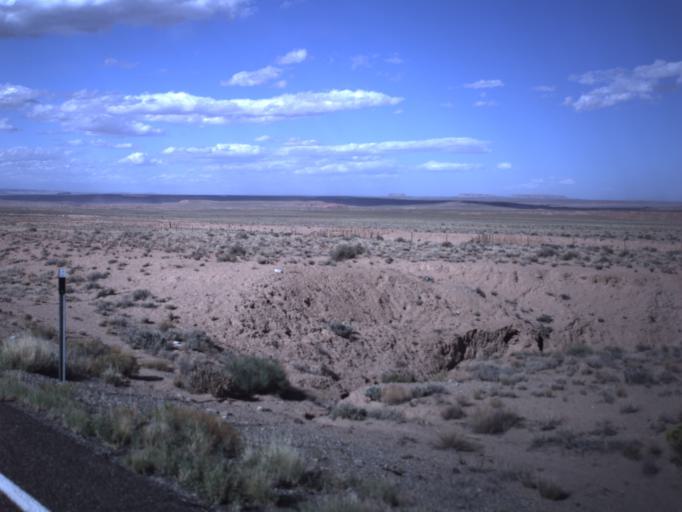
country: US
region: Utah
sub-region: Emery County
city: Ferron
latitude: 38.2776
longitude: -110.6614
